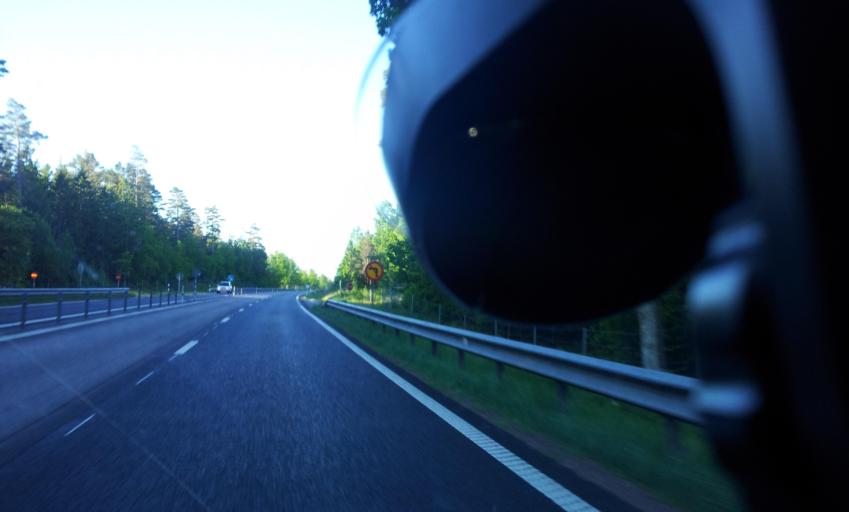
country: SE
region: Kalmar
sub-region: Monsteras Kommun
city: Timmernabben
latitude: 56.8862
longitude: 16.3822
